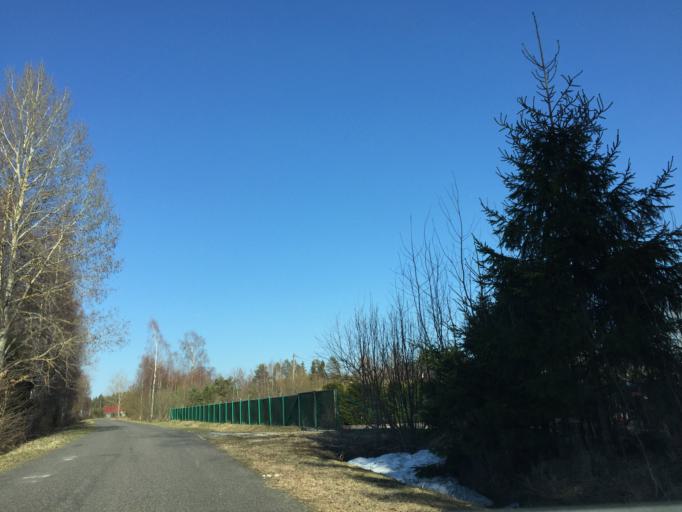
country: EE
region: Ida-Virumaa
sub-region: Johvi vald
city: Johvi
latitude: 59.0113
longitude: 27.5141
